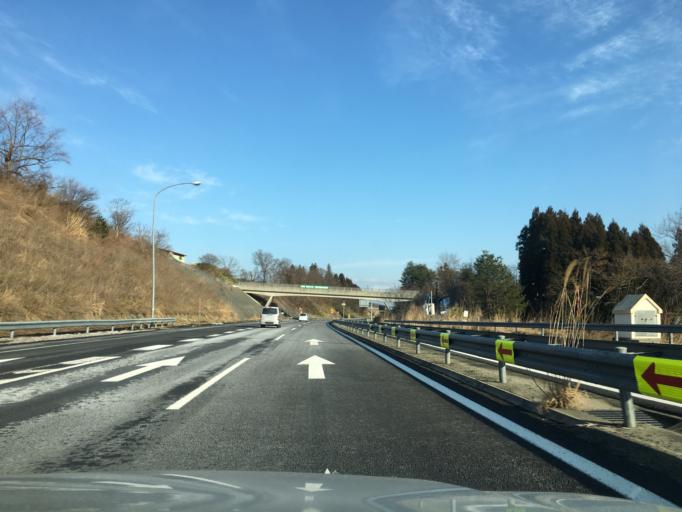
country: JP
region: Yamagata
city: Sagae
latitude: 38.4234
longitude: 140.1674
